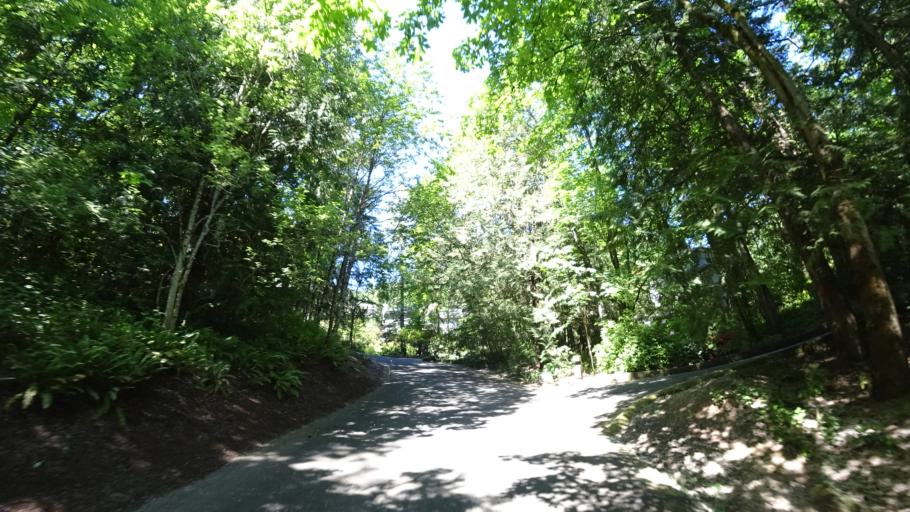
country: US
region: Oregon
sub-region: Washington County
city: West Slope
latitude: 45.4991
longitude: -122.7260
